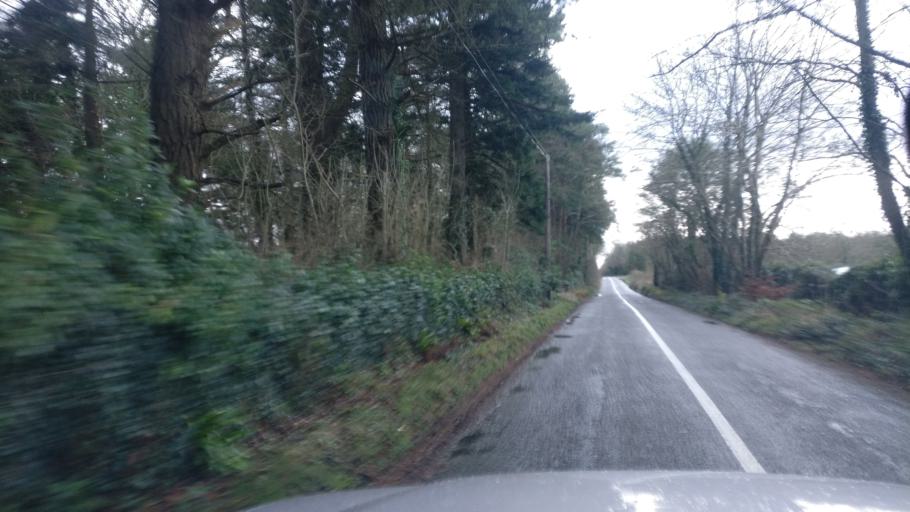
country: IE
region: Connaught
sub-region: County Galway
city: Loughrea
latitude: 53.2476
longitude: -8.6223
